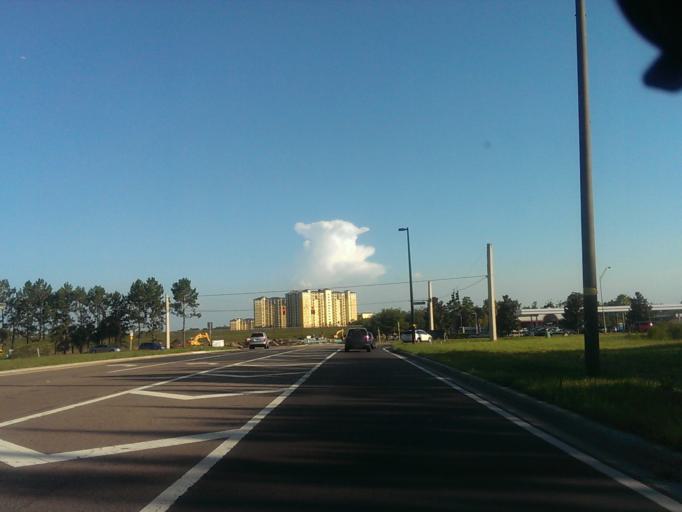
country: US
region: Florida
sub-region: Osceola County
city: Celebration
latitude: 28.3592
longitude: -81.4873
